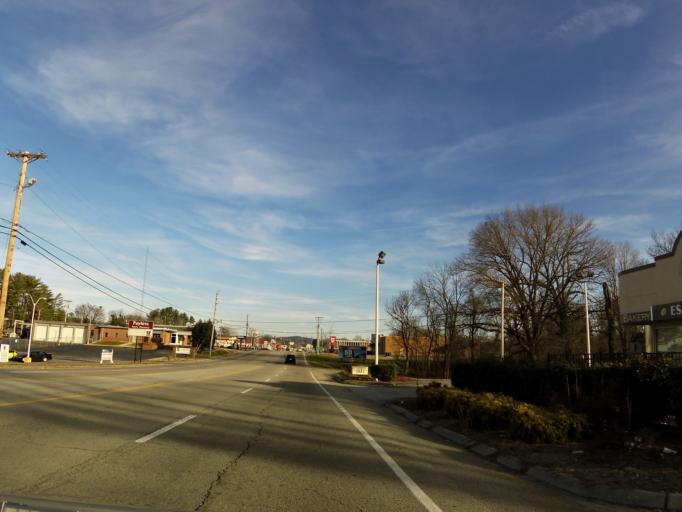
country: US
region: Tennessee
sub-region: White County
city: Sparta
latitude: 35.9331
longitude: -85.4788
